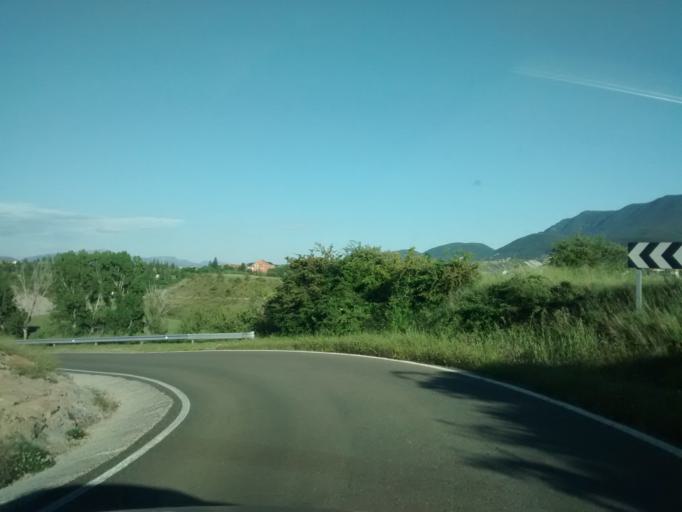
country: ES
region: Aragon
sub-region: Provincia de Huesca
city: Jaca
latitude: 42.5751
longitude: -0.5681
